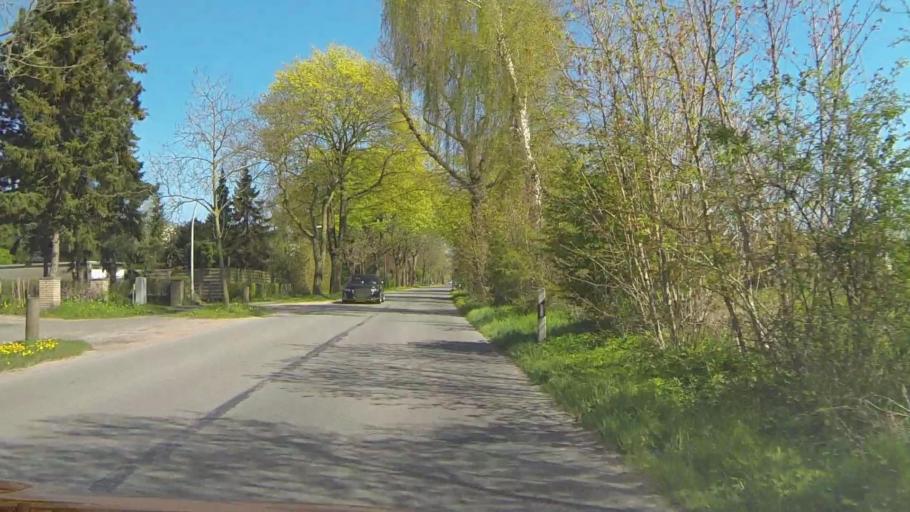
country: DE
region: Schleswig-Holstein
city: Moorrege
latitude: 53.6786
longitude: 9.6913
